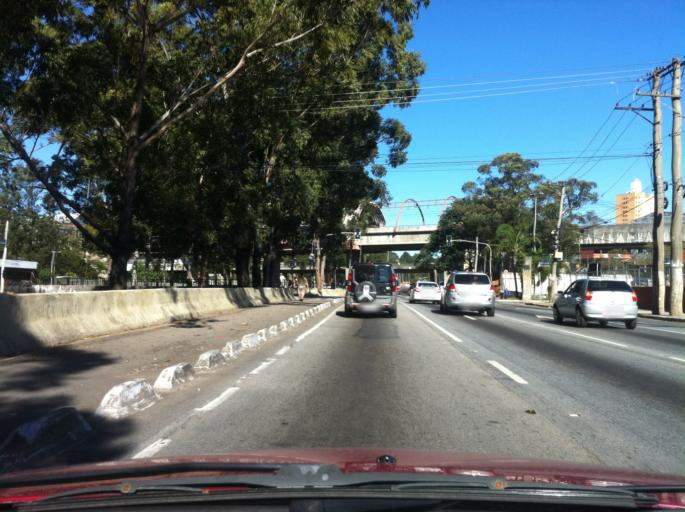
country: BR
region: Sao Paulo
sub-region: Ferraz De Vasconcelos
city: Ferraz de Vasconcelos
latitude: -23.5405
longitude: -46.4497
